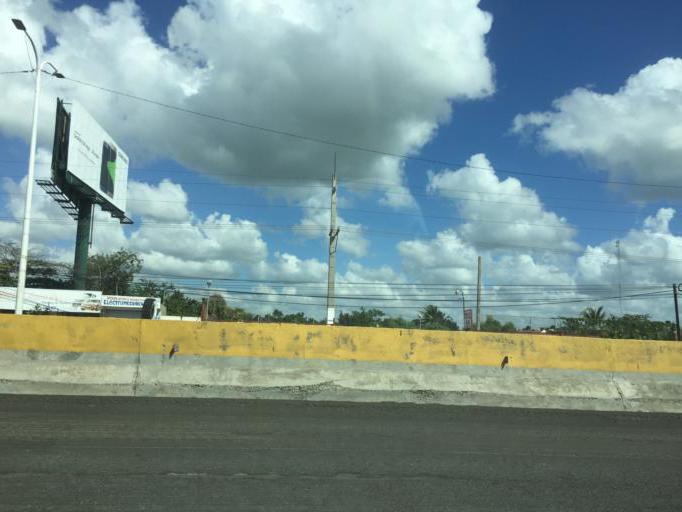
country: DO
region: Santo Domingo
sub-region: Santo Domingo
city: Boca Chica
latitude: 18.4547
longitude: -69.6970
